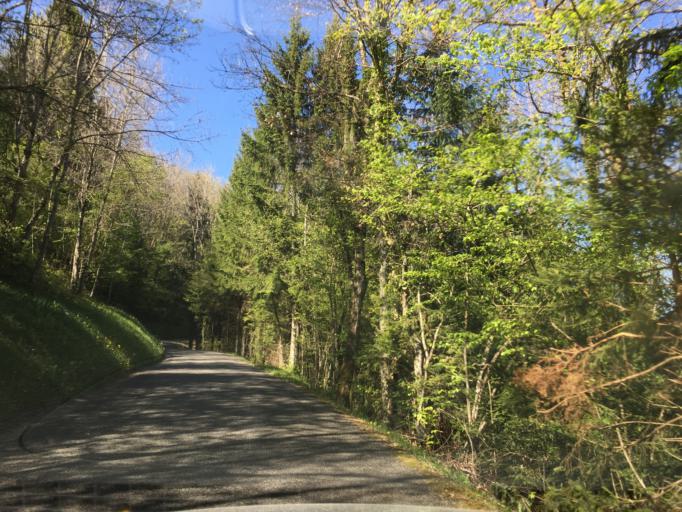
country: FR
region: Rhone-Alpes
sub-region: Departement de la Savoie
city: La Motte-Servolex
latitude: 45.5815
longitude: 5.8307
